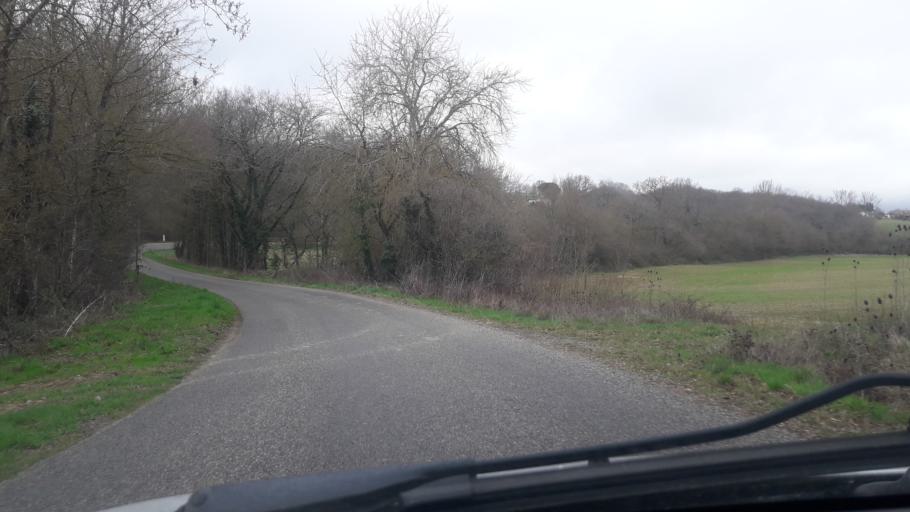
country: FR
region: Midi-Pyrenees
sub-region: Departement du Gers
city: Gimont
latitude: 43.6560
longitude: 0.9775
